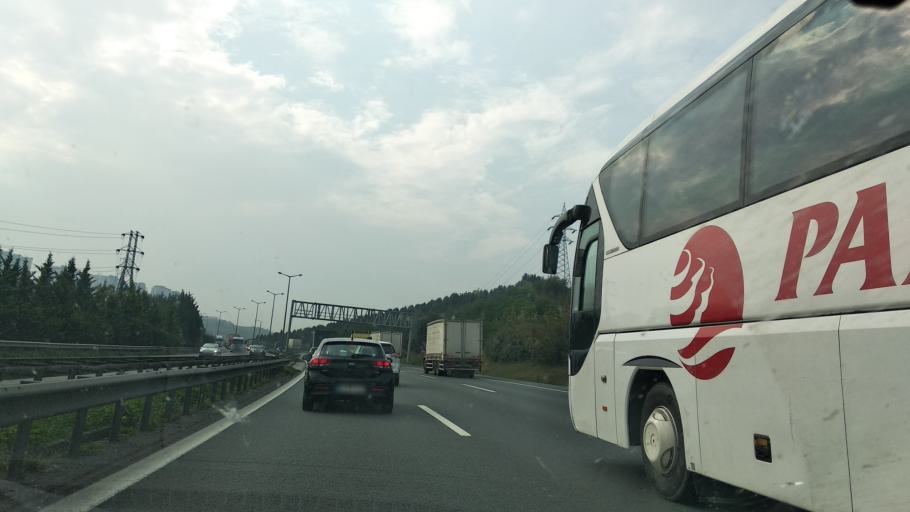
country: TR
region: Kocaeli
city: Izmit
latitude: 40.7863
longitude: 29.9507
